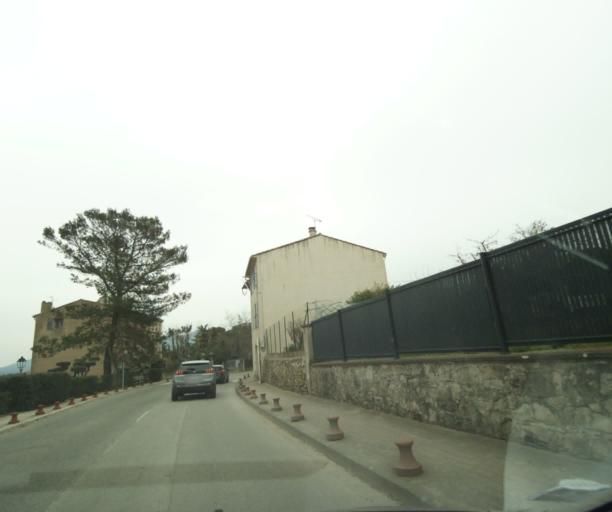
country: FR
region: Provence-Alpes-Cote d'Azur
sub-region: Departement des Bouches-du-Rhone
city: Peynier
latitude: 43.4466
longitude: 5.6410
